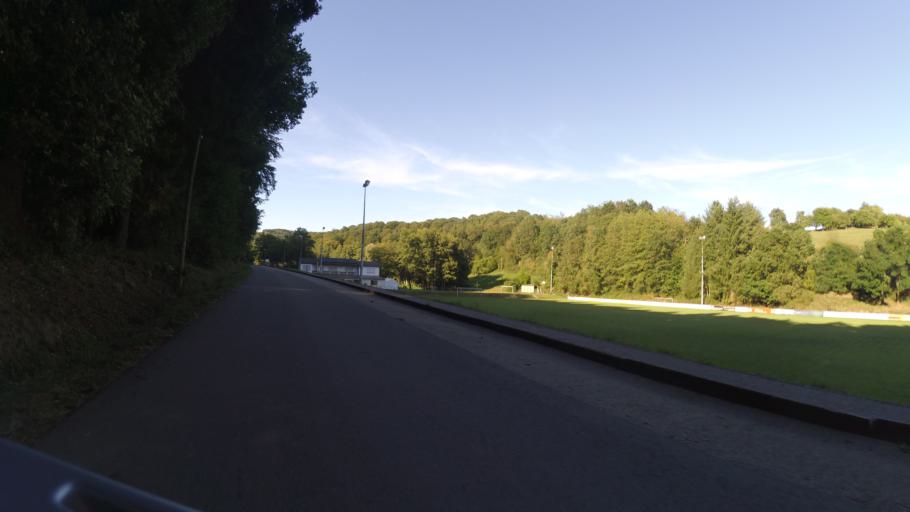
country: DE
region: Saarland
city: Lebach
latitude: 49.4420
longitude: 6.9412
